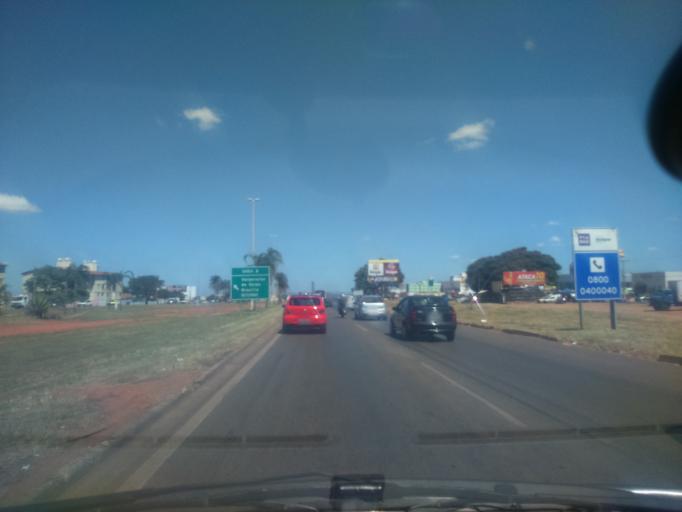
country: BR
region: Goias
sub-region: Luziania
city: Luziania
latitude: -16.0720
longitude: -47.9853
